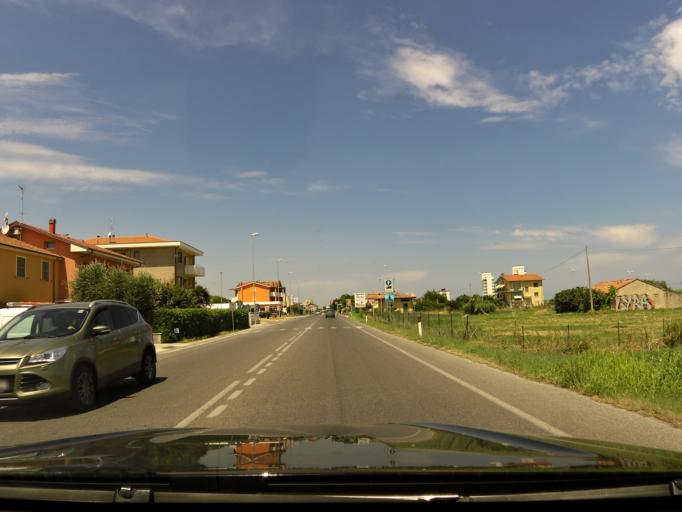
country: IT
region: The Marches
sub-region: Provincia di Pesaro e Urbino
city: Marotta
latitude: 43.7545
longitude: 13.1608
